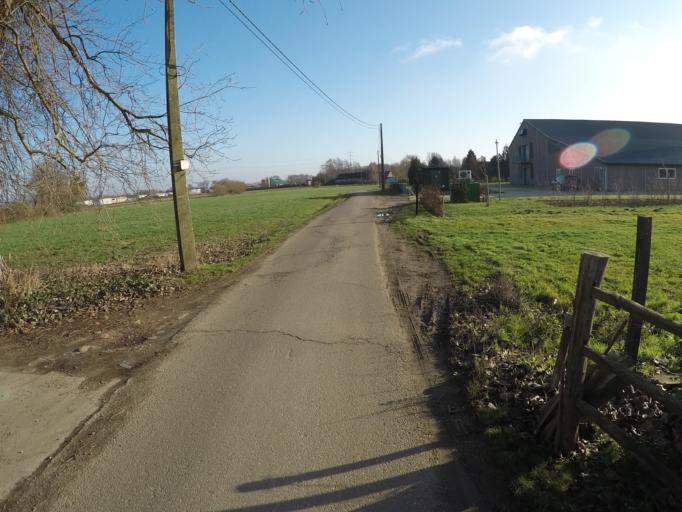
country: BE
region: Flanders
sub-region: Provincie Antwerpen
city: Ranst
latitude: 51.2093
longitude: 4.5686
